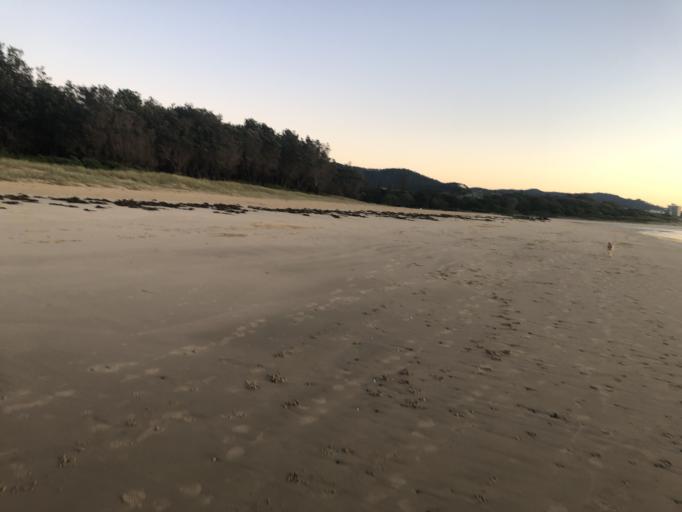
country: AU
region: New South Wales
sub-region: Coffs Harbour
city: Coffs Harbour
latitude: -30.2989
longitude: 153.1400
